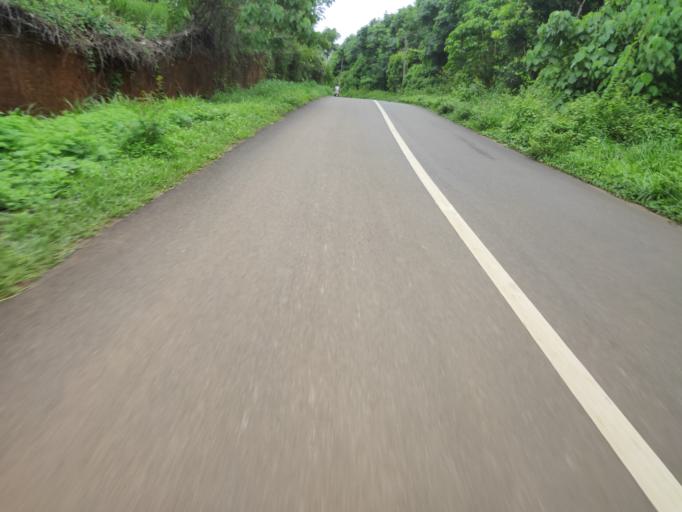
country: IN
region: Kerala
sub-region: Malappuram
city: Manjeri
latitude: 11.1709
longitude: 76.1801
